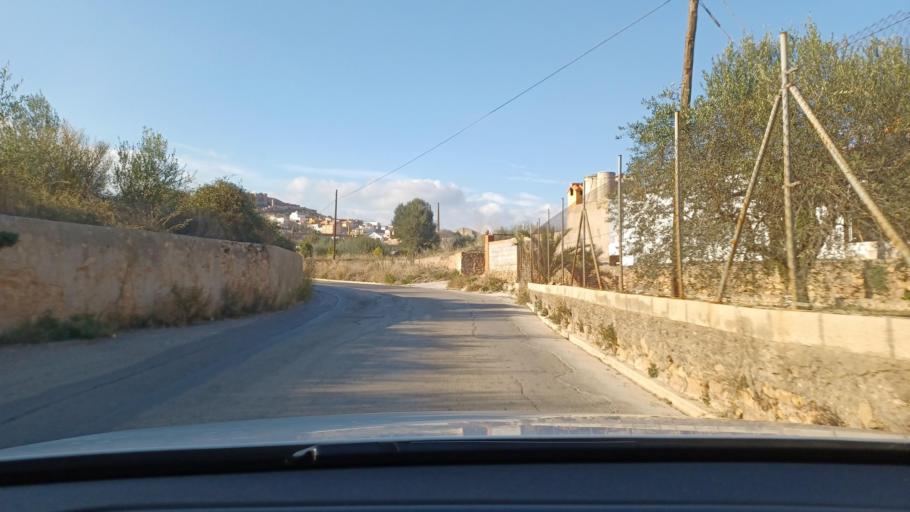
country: ES
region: Valencia
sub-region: Provincia de Castello
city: Onda
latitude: 39.9593
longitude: -0.2513
